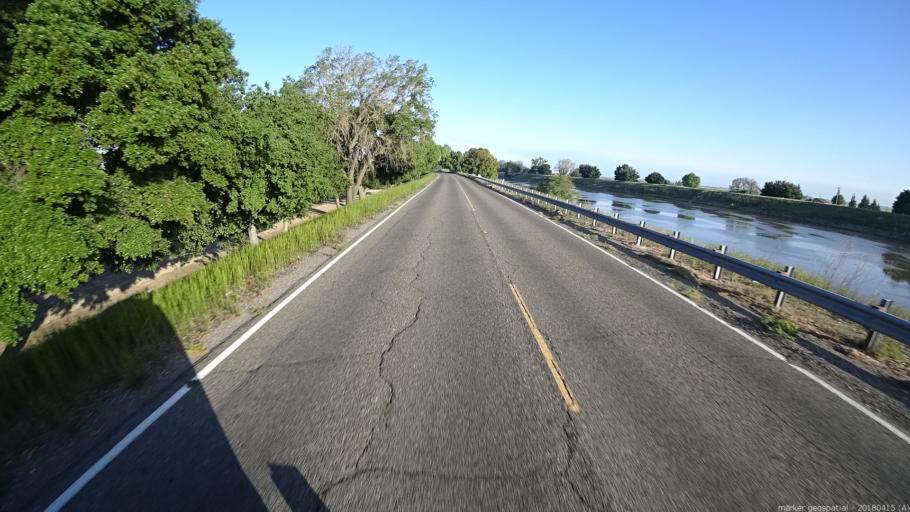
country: US
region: California
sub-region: Sacramento County
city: Walnut Grove
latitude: 38.2806
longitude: -121.5484
